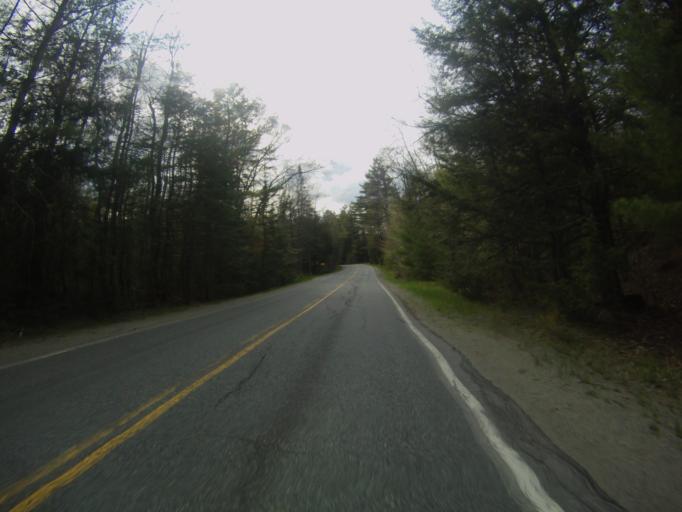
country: US
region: New York
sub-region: Warren County
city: Warrensburg
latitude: 43.8451
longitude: -73.8187
